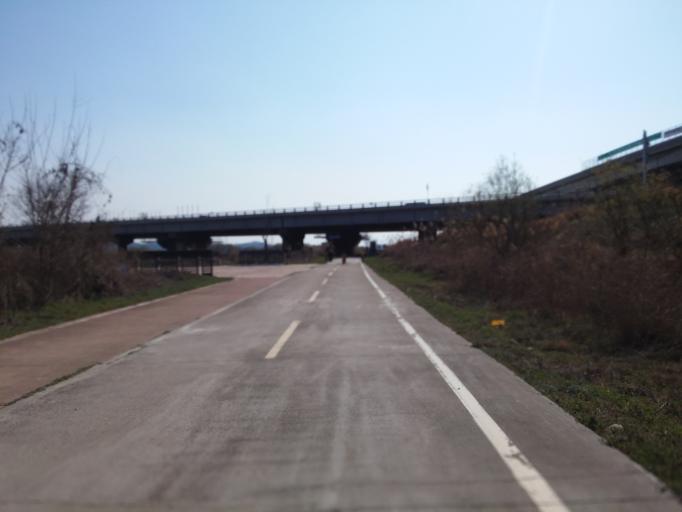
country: KR
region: Chungcheongbuk-do
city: Cheongju-si
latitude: 36.6528
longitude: 127.3744
